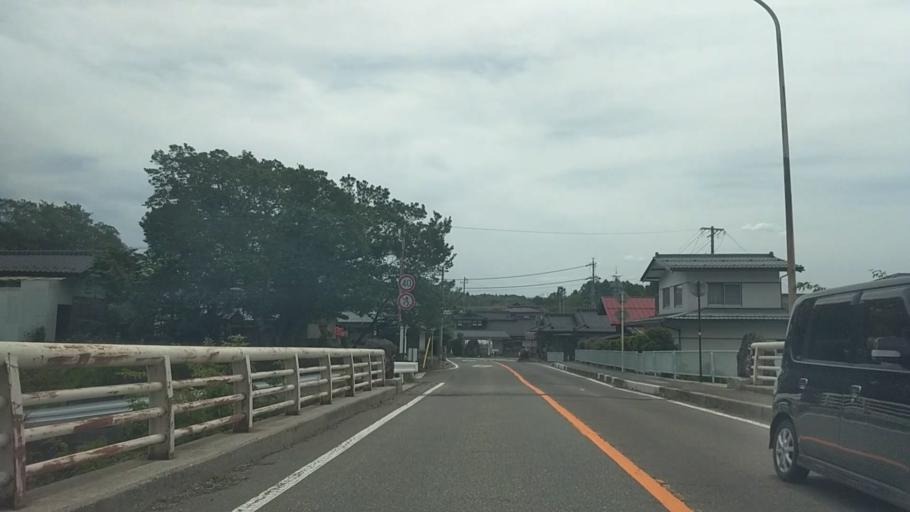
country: JP
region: Nagano
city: Chino
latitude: 36.0315
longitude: 138.2472
